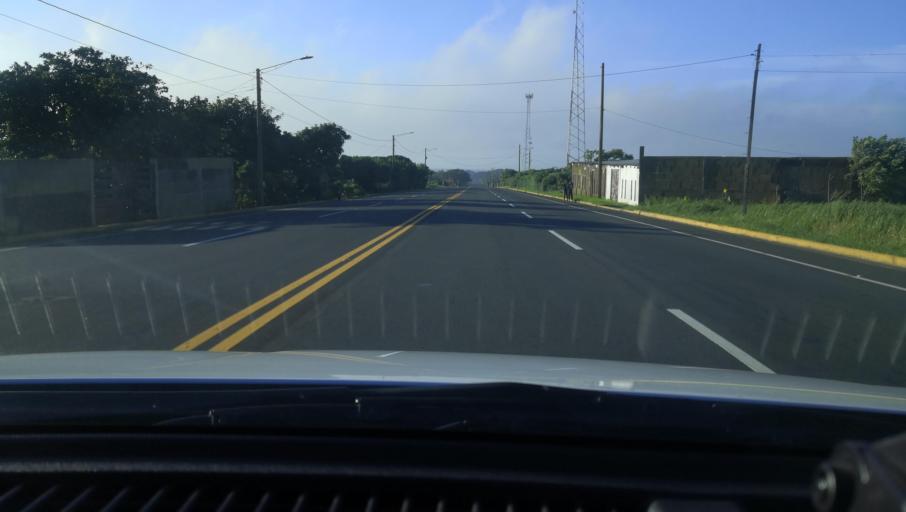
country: NI
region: Managua
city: El Crucero
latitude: 11.9271
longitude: -86.2852
